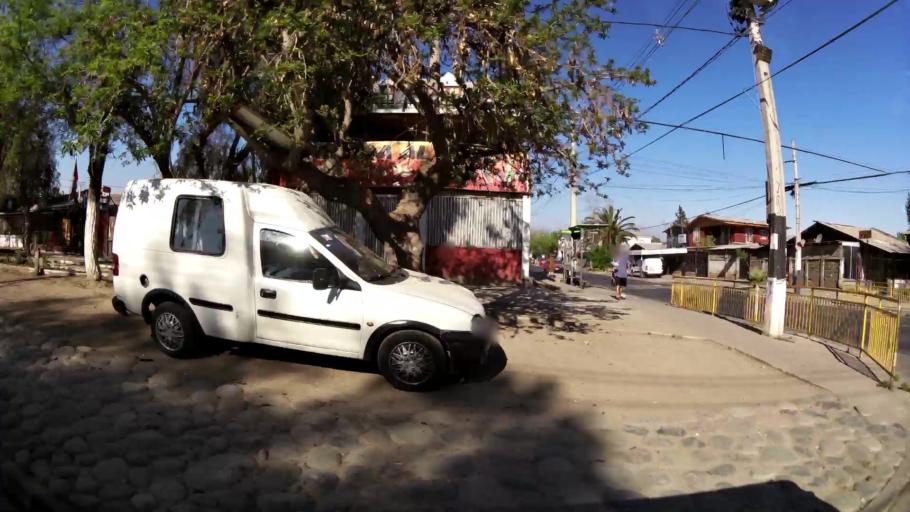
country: CL
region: Santiago Metropolitan
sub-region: Provincia de Santiago
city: La Pintana
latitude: -33.5786
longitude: -70.6492
